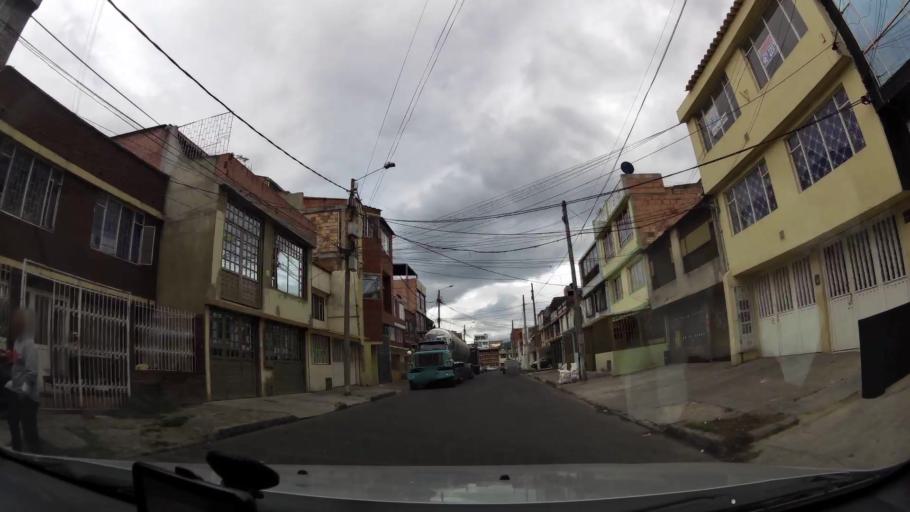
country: CO
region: Bogota D.C.
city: Bogota
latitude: 4.6071
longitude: -74.1396
